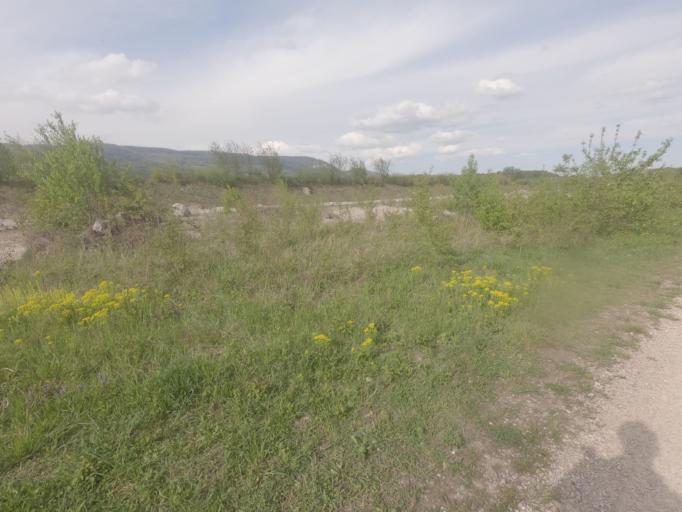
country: CH
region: Bern
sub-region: Oberaargau
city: Attiswil
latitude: 47.2316
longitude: 7.5998
